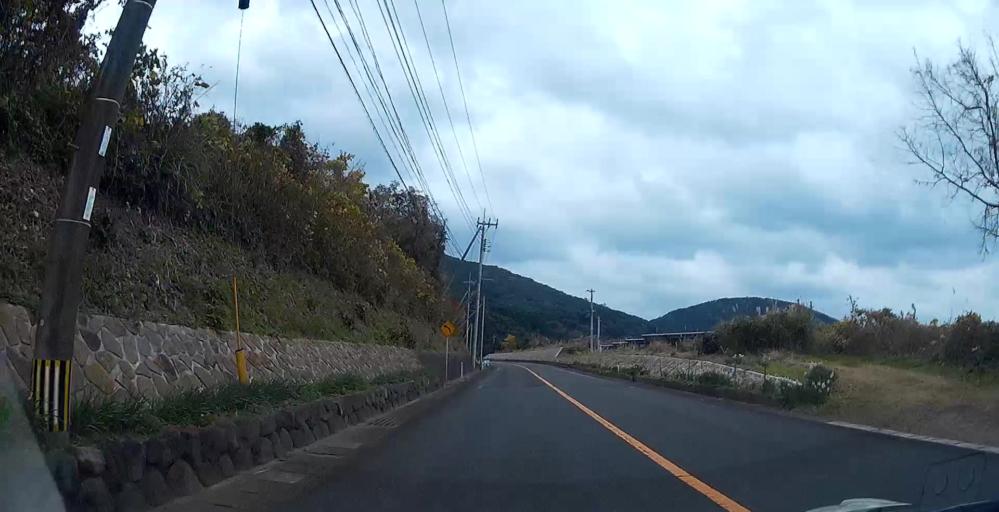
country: JP
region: Kagoshima
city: Akune
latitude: 32.1059
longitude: 130.1486
